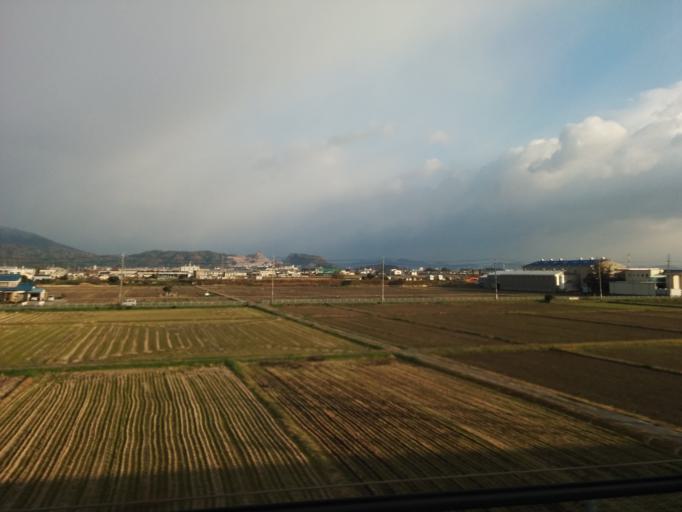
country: JP
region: Gifu
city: Tarui
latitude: 35.3496
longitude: 136.5663
